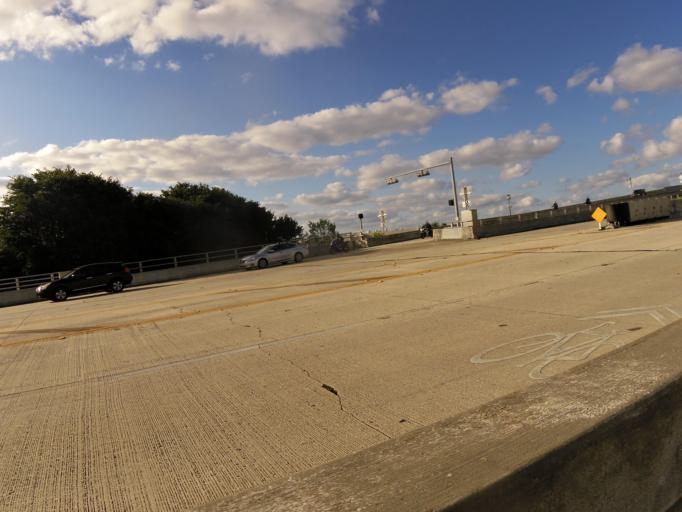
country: US
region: Florida
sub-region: Duval County
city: Jacksonville
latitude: 30.3245
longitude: -81.6681
